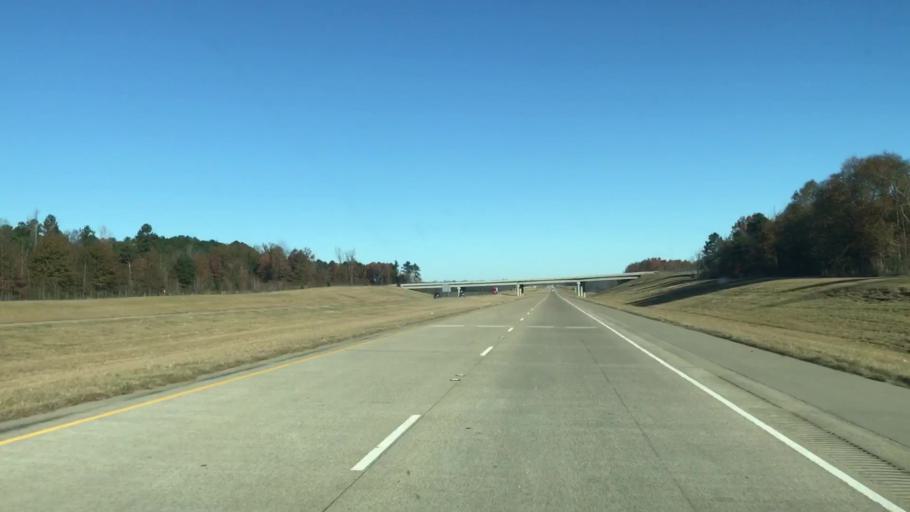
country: US
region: Louisiana
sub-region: Caddo Parish
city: Blanchard
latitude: 32.6126
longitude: -93.8348
